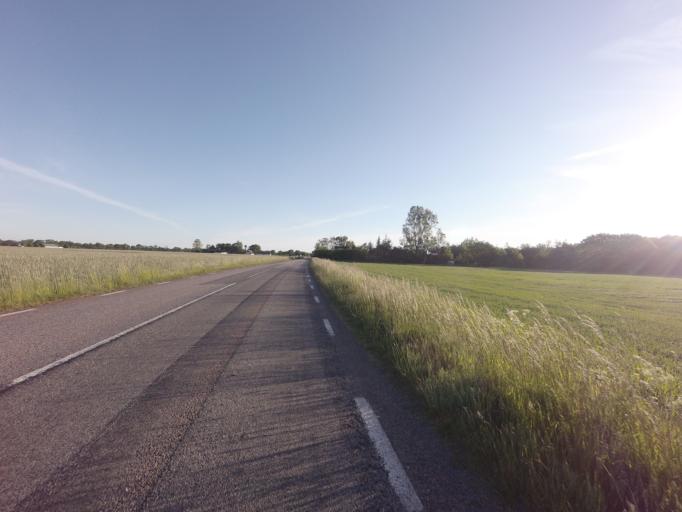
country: SE
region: Skane
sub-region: Helsingborg
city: Odakra
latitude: 56.1987
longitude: 12.6745
